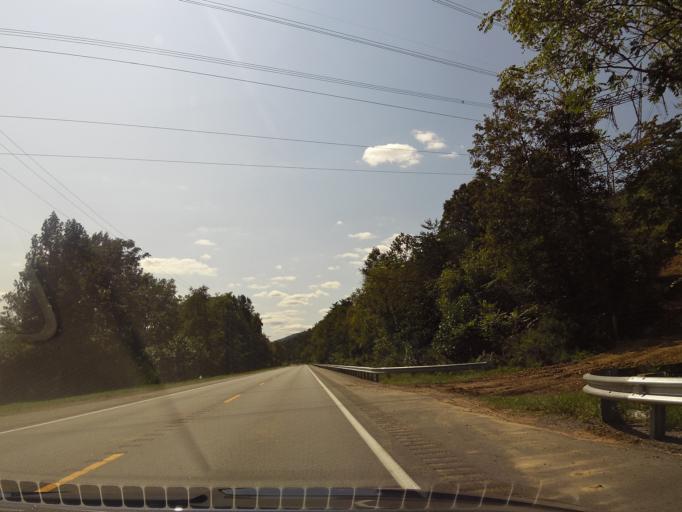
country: US
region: Kentucky
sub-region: Bell County
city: Pineville
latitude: 36.7924
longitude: -83.5446
